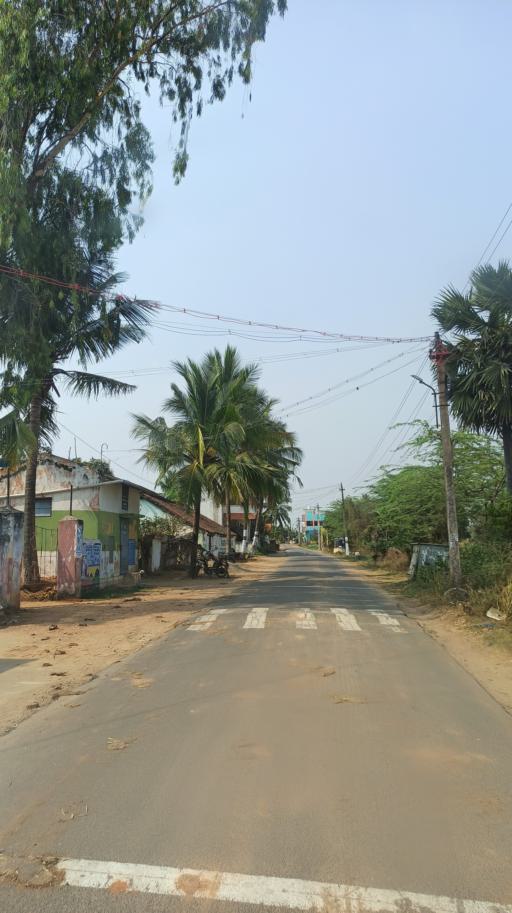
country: IN
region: Tamil Nadu
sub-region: Tiruvannamalai
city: Desur
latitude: 12.4524
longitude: 79.3727
